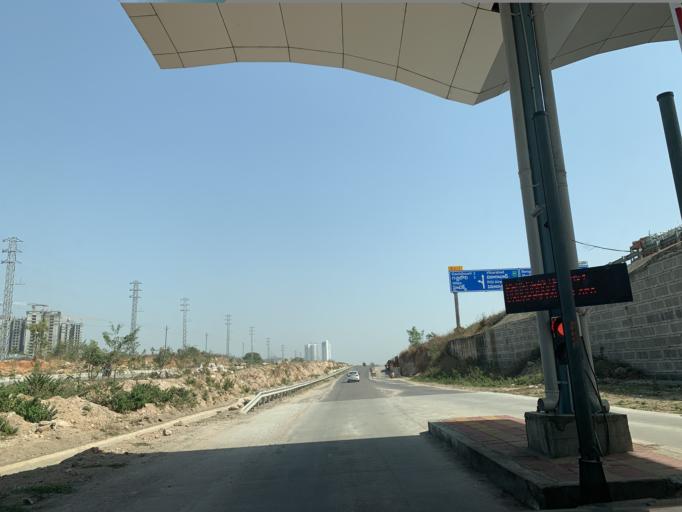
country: IN
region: Telangana
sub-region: Medak
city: Serilingampalle
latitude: 17.4070
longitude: 78.3315
